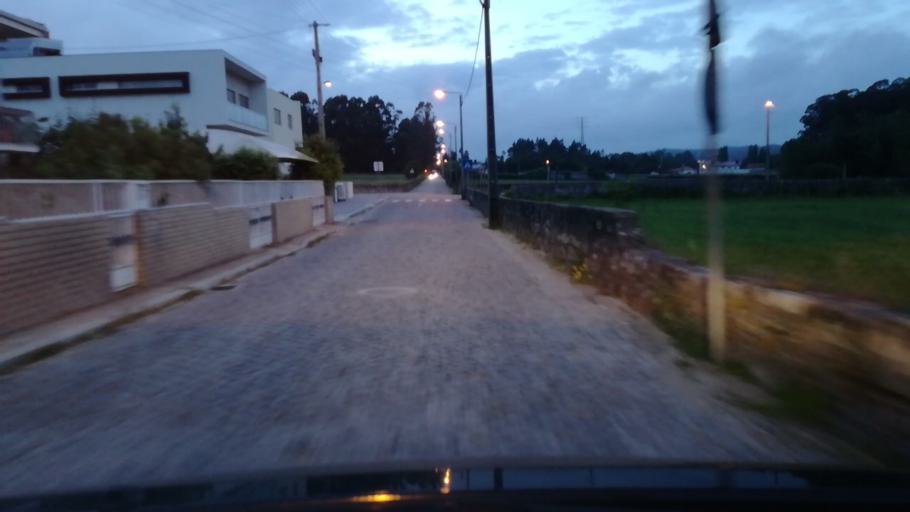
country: PT
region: Porto
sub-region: Maia
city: Anta
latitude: 41.2561
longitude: -8.6086
